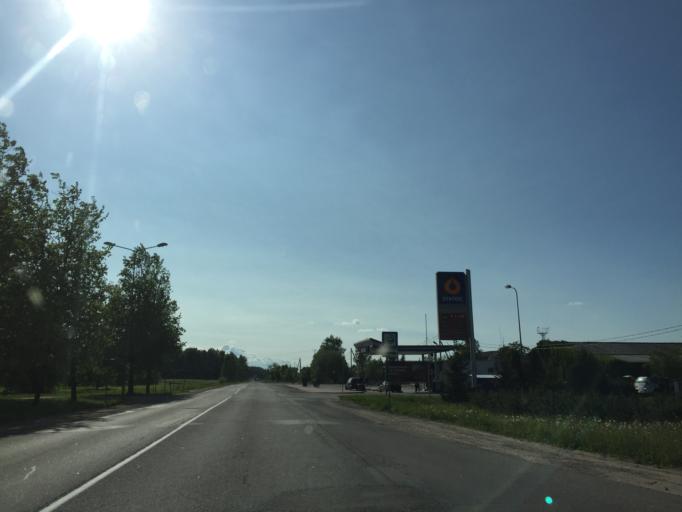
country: LV
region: Salaspils
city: Salaspils
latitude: 56.8215
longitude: 24.4156
